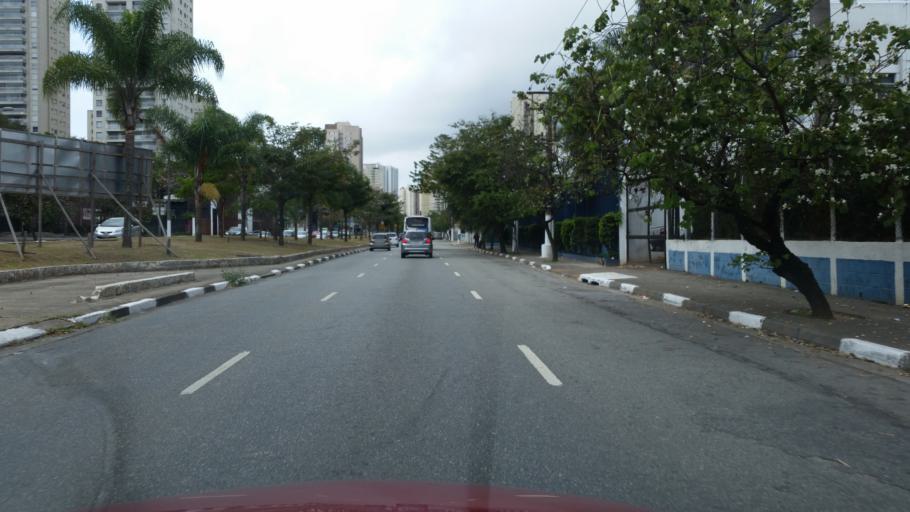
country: BR
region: Sao Paulo
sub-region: Diadema
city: Diadema
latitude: -23.6682
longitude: -46.6953
